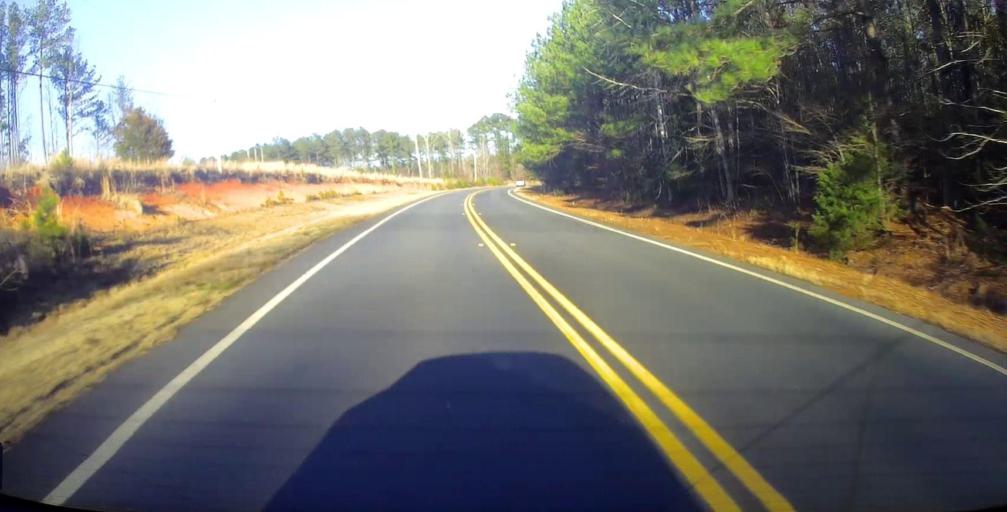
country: US
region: Georgia
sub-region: Harris County
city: Pine Mountain
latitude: 32.9155
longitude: -84.7985
